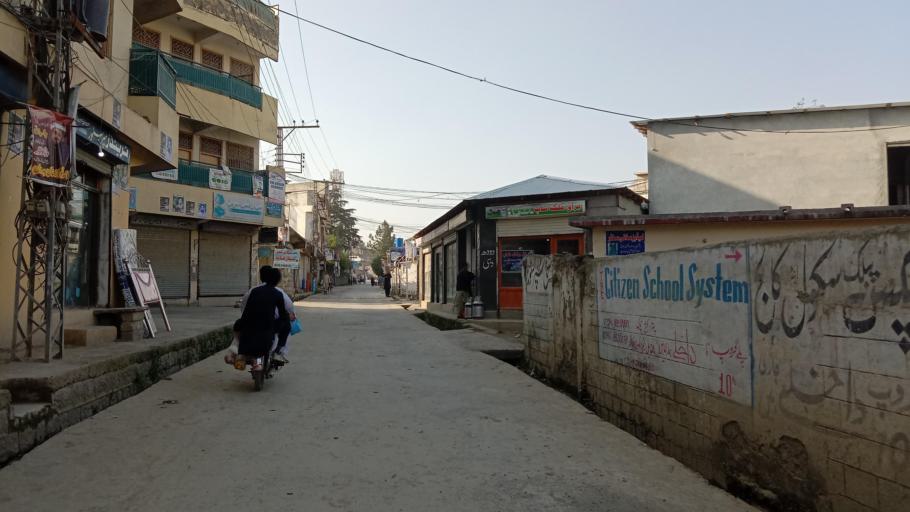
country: PK
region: Khyber Pakhtunkhwa
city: Abbottabad
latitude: 34.1985
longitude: 73.2286
